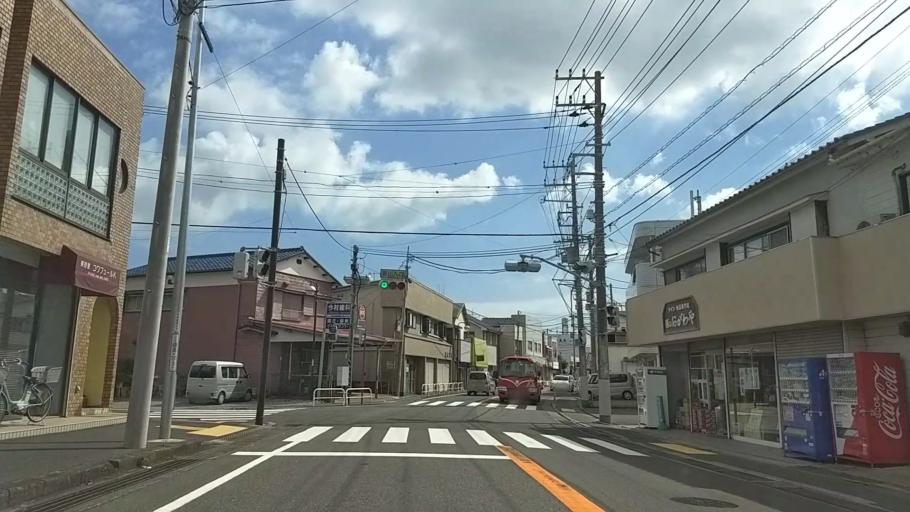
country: JP
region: Kanagawa
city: Miura
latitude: 35.1495
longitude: 139.6279
